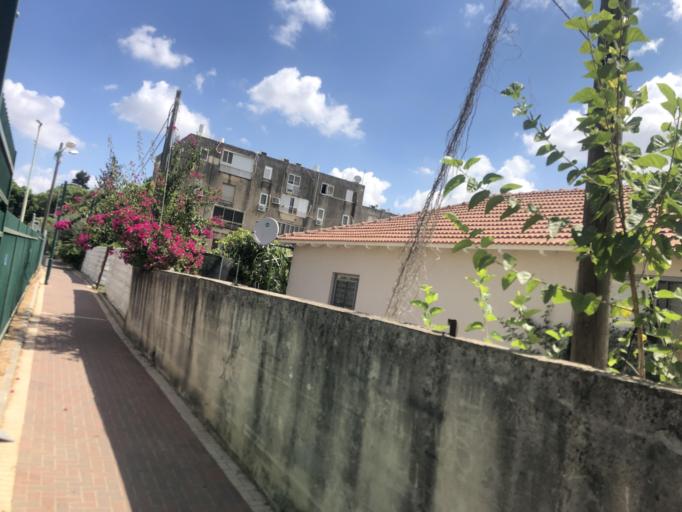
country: IL
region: Central District
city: Yehud
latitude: 32.0296
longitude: 34.8949
